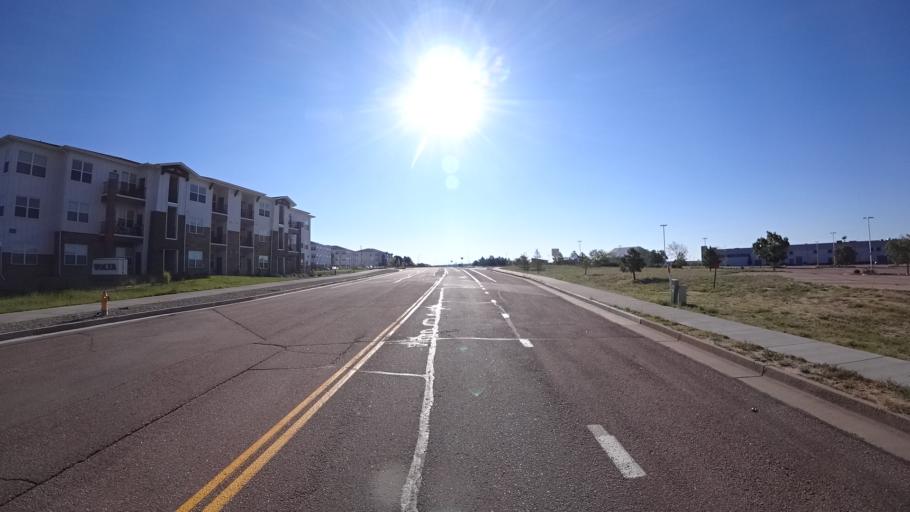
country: US
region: Colorado
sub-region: El Paso County
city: Gleneagle
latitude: 38.9944
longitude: -104.7966
